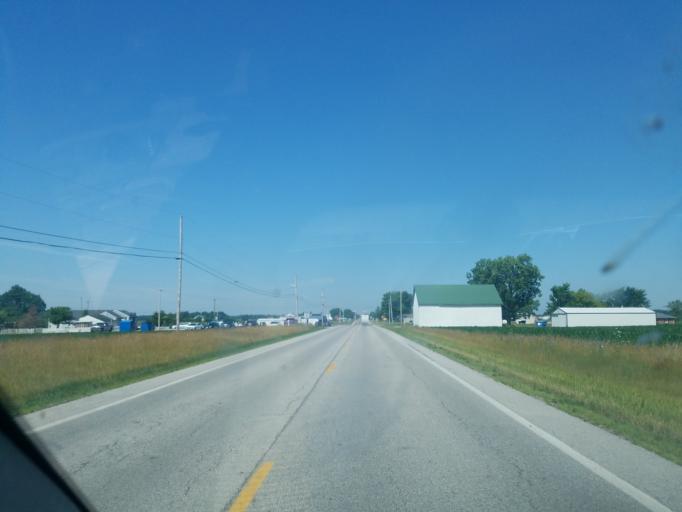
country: US
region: Ohio
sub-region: Shelby County
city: Botkins
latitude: 40.4388
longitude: -84.1760
